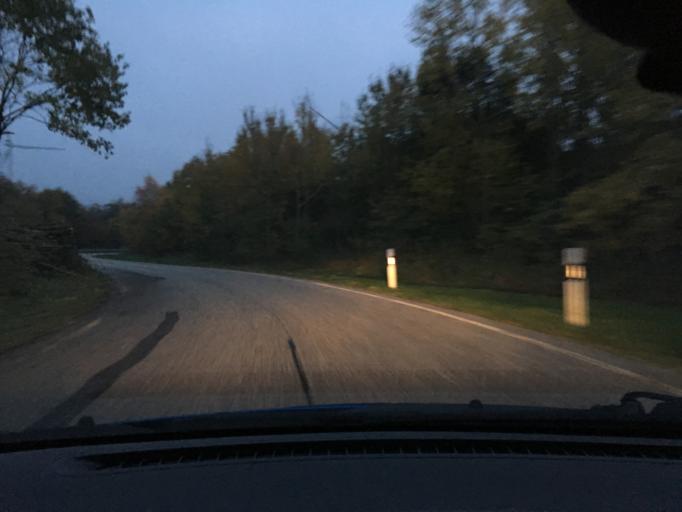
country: DE
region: Schleswig-Holstein
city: Arkebek
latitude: 54.1384
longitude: 9.2477
